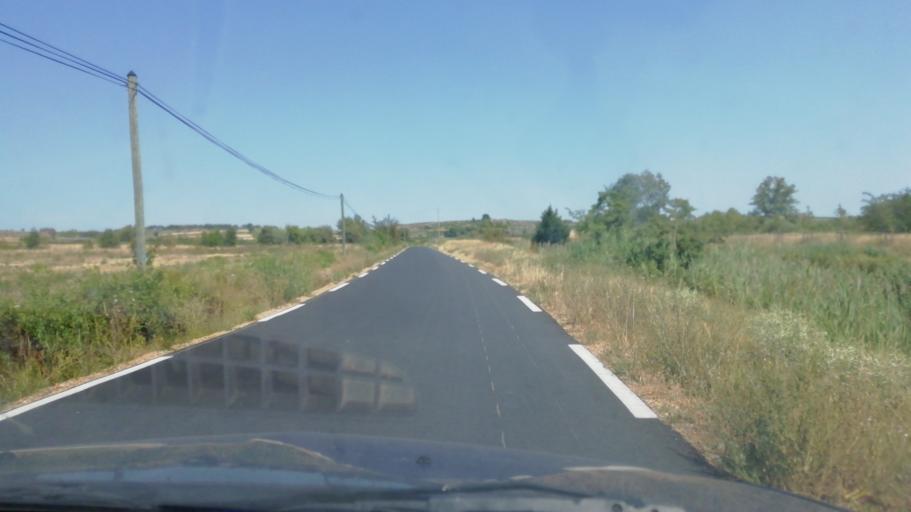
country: FR
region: Languedoc-Roussillon
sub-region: Departement de l'Herault
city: Capestang
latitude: 43.3306
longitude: 3.0524
